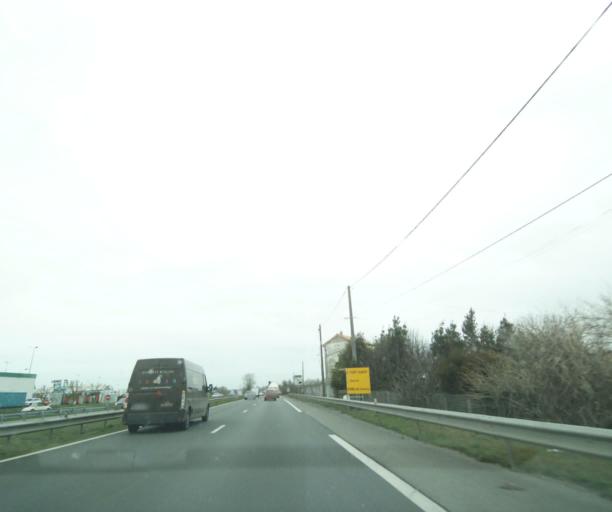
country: FR
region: Poitou-Charentes
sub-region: Departement de la Charente-Maritime
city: Angoulins
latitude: 46.1102
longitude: -1.1006
